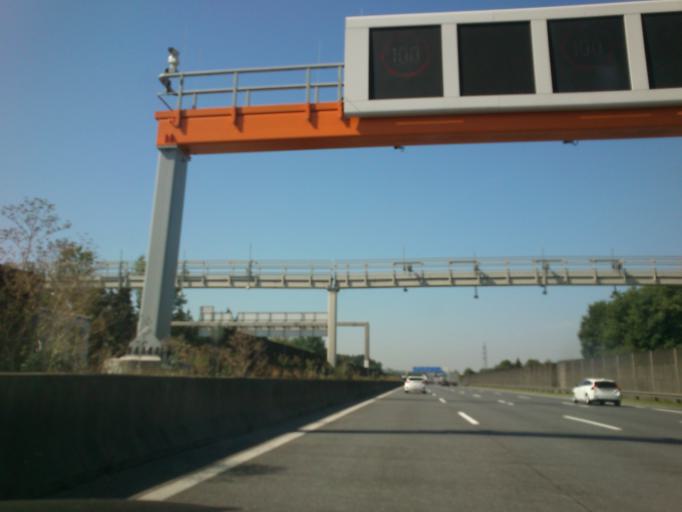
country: AT
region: Upper Austria
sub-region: Politischer Bezirk Linz-Land
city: Traun
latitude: 48.1971
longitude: 14.2460
